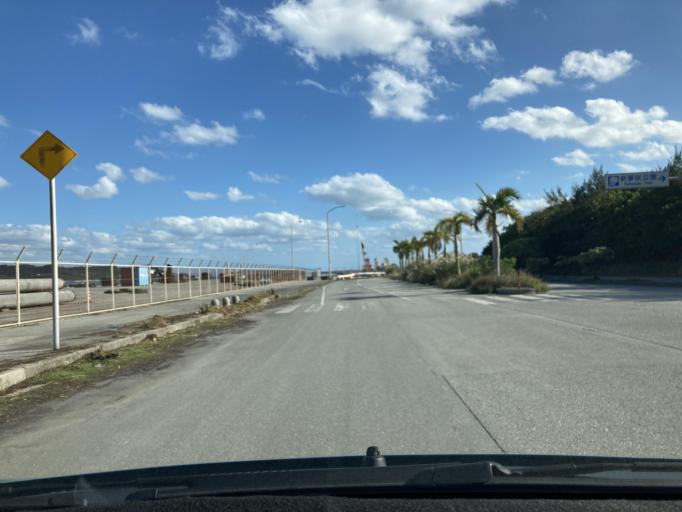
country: JP
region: Okinawa
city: Katsuren-haebaru
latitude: 26.3287
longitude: 127.8565
